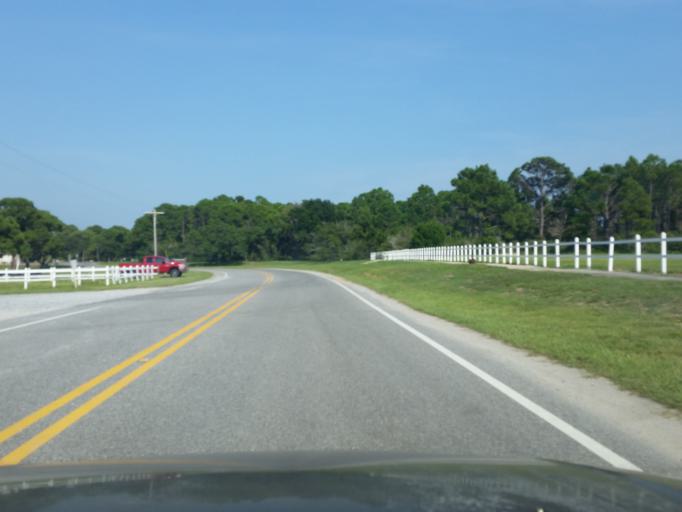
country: US
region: Alabama
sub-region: Mobile County
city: Dauphin Island
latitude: 30.2310
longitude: -88.0178
